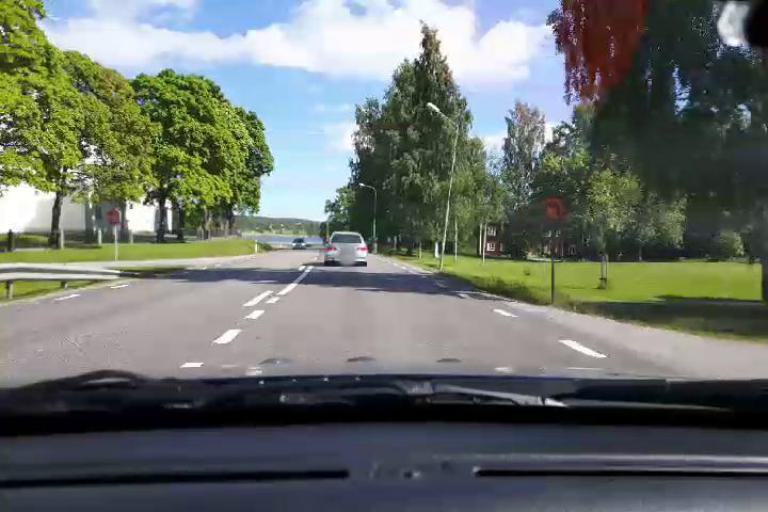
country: SE
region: Gaevleborg
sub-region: Hudiksvalls Kommun
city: Sorforsa
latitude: 61.7341
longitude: 16.9378
